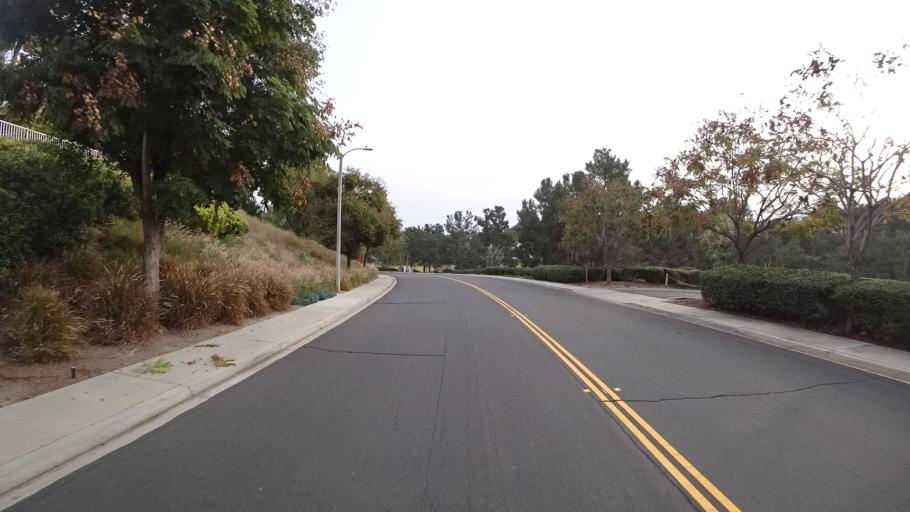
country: US
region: California
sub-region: Orange County
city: Laguna Woods
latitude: 33.5943
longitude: -117.7221
